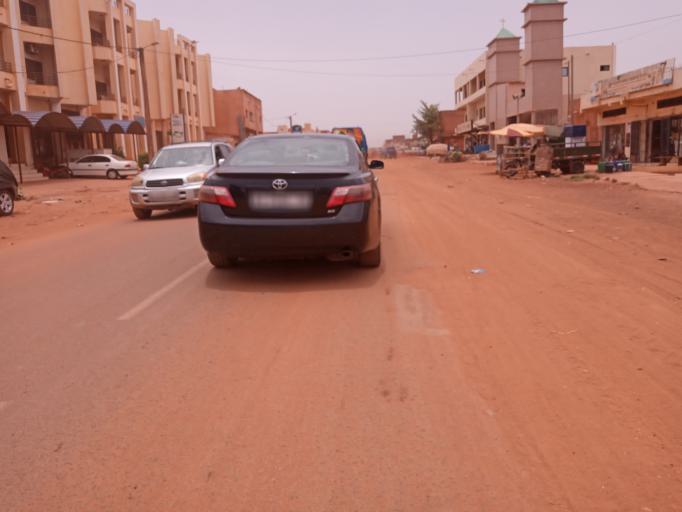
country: ML
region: Bamako
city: Bamako
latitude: 12.5795
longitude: -8.0165
